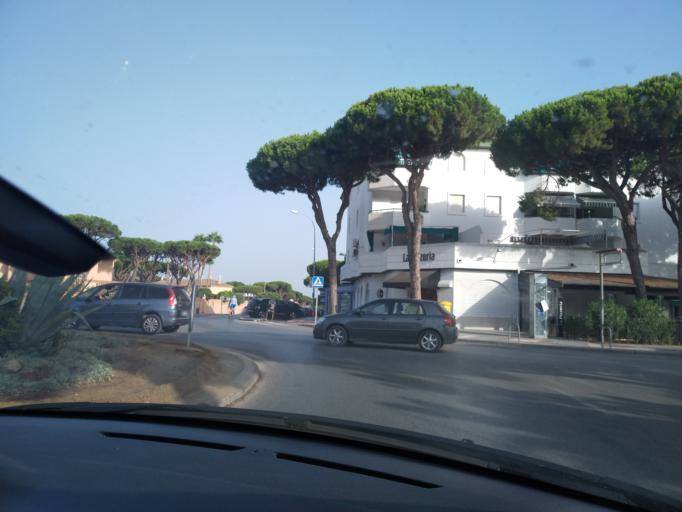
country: ES
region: Andalusia
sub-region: Provincia de Cadiz
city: Chiclana de la Frontera
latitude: 36.3769
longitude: -6.1873
